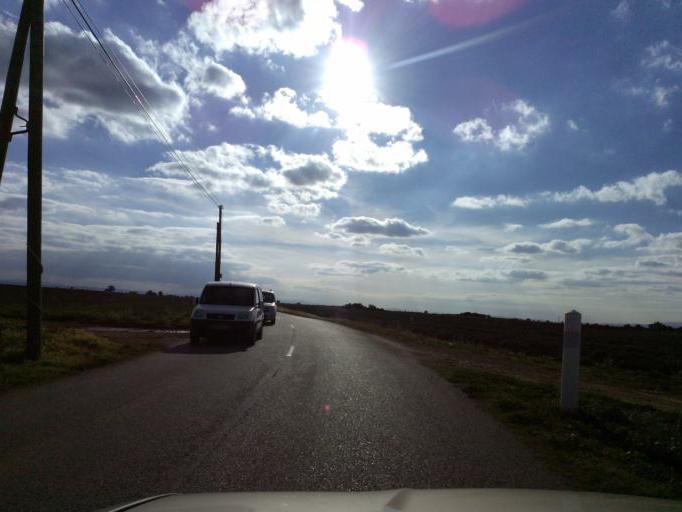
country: FR
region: Provence-Alpes-Cote d'Azur
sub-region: Departement des Alpes-de-Haute-Provence
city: Valensole
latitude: 43.8668
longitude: 6.0108
